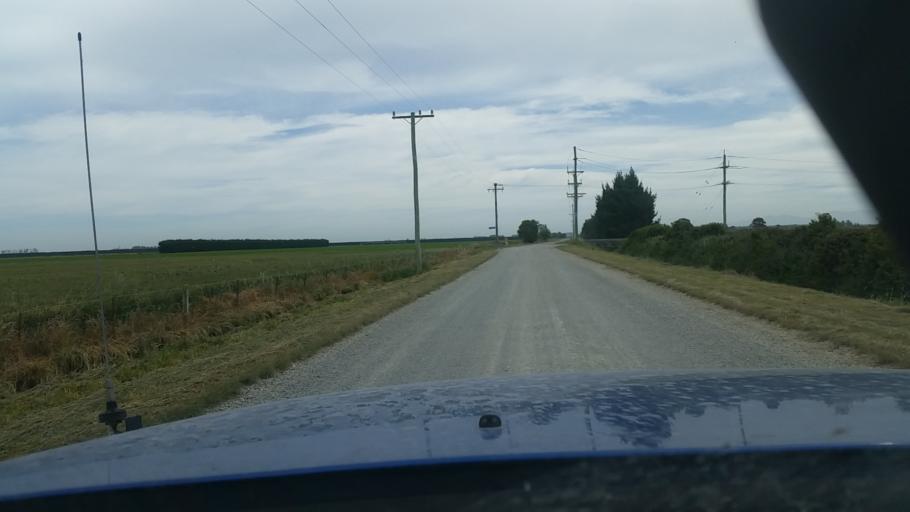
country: NZ
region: Canterbury
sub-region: Ashburton District
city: Tinwald
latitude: -44.0069
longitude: 171.7722
